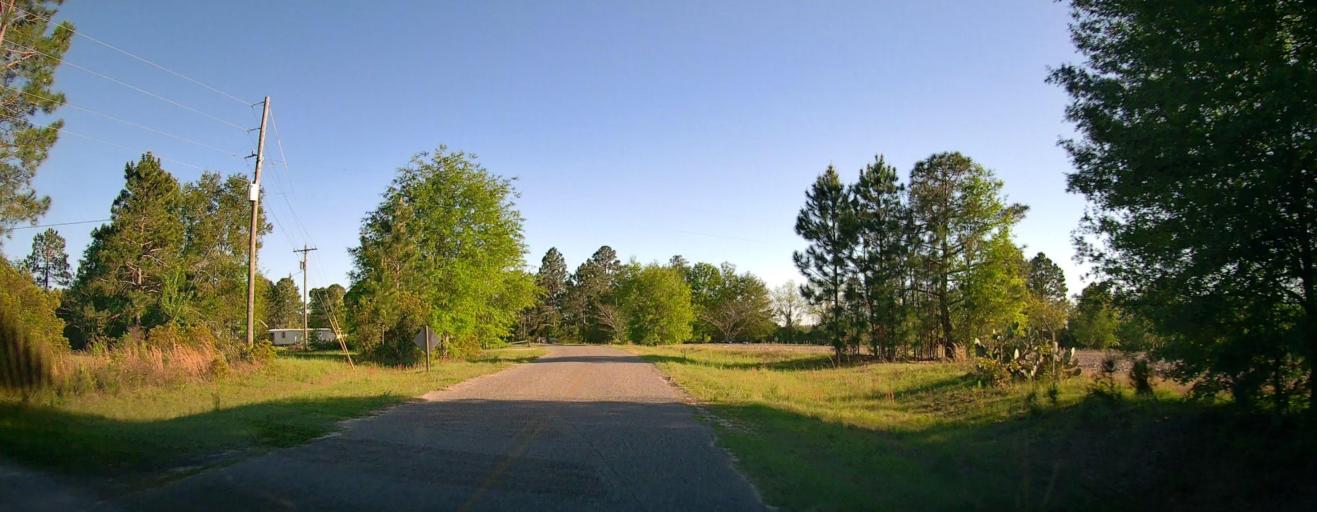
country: US
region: Georgia
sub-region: Ben Hill County
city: Fitzgerald
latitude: 31.6901
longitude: -83.1537
